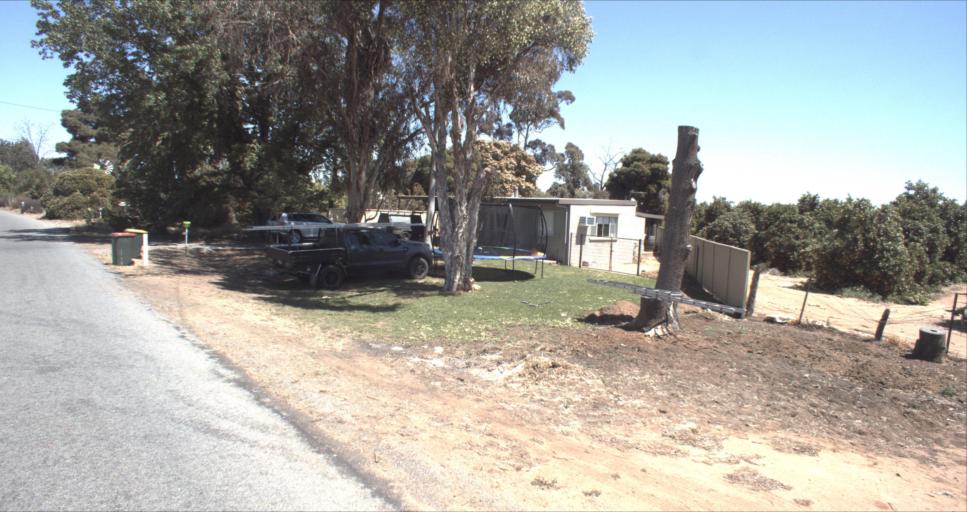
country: AU
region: New South Wales
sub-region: Leeton
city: Leeton
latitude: -34.5418
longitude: 146.3947
